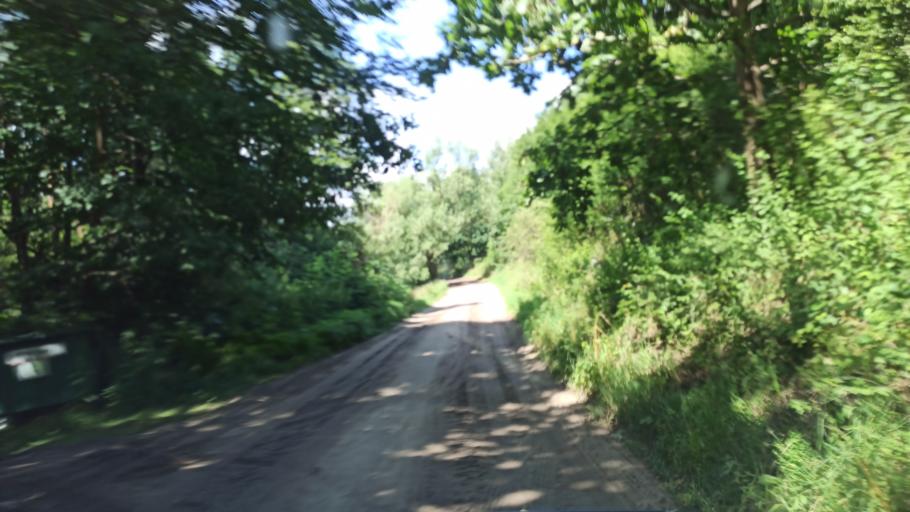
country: PL
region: Warmian-Masurian Voivodeship
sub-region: Powiat ostrodzki
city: Morag
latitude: 53.8627
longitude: 20.0589
